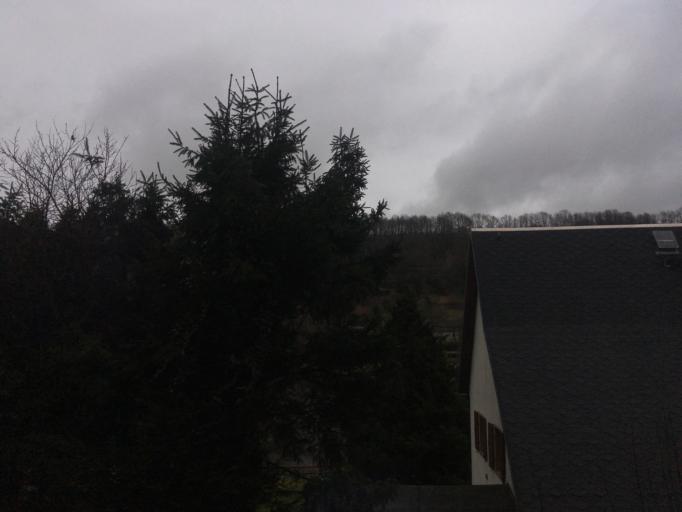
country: DE
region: Saxony
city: Pirna
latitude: 50.9565
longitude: 13.9760
